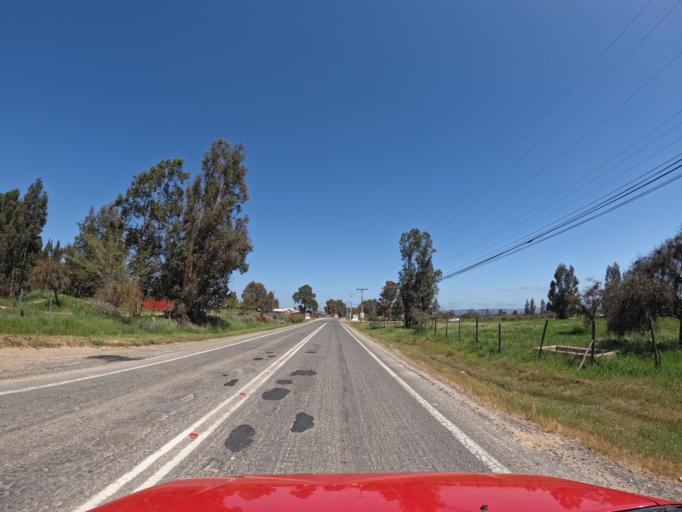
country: CL
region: O'Higgins
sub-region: Provincia de Colchagua
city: Santa Cruz
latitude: -34.7327
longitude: -71.6841
